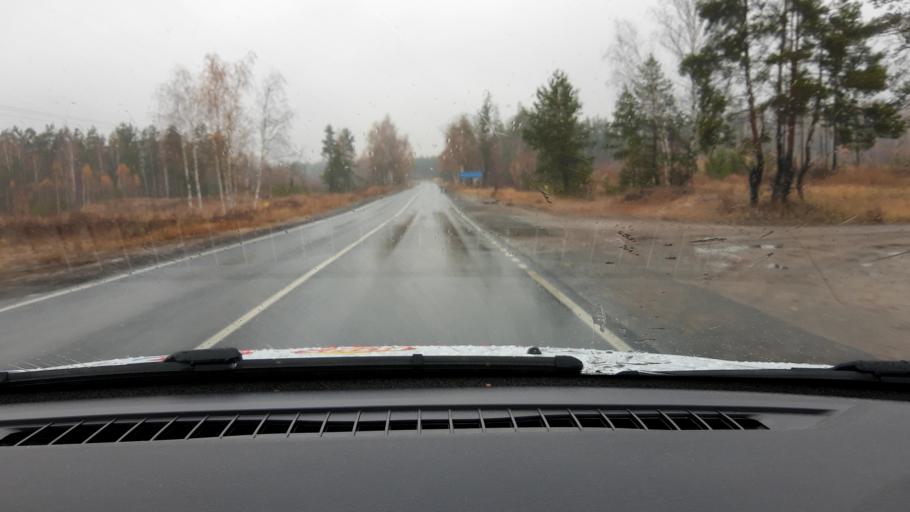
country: RU
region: Nizjnij Novgorod
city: Babino
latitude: 56.2943
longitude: 43.5978
